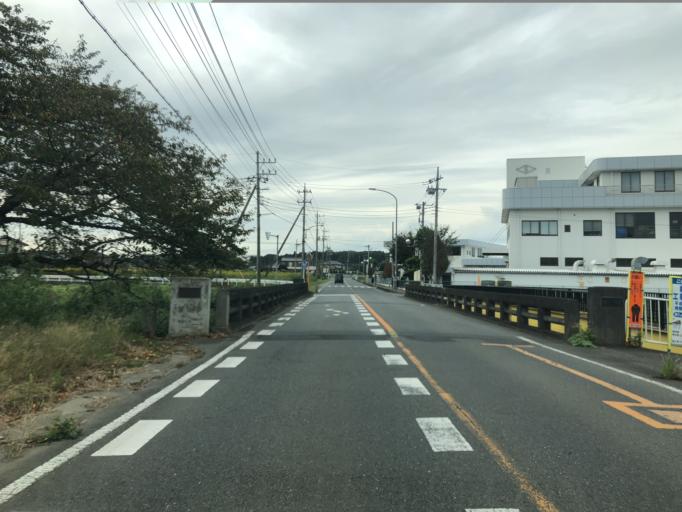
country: JP
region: Saitama
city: Fukiage-fujimi
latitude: 36.0584
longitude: 139.3945
